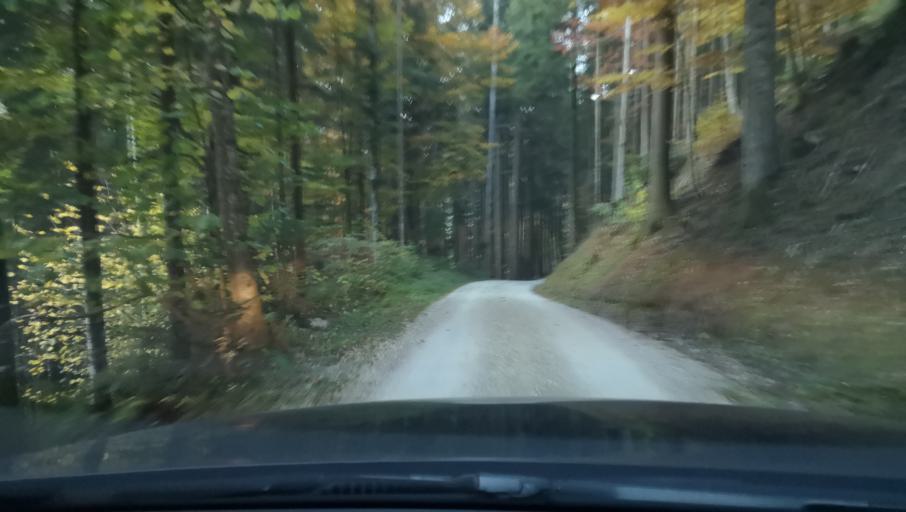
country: AT
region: Styria
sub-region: Politischer Bezirk Weiz
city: Birkfeld
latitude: 47.3660
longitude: 15.6562
